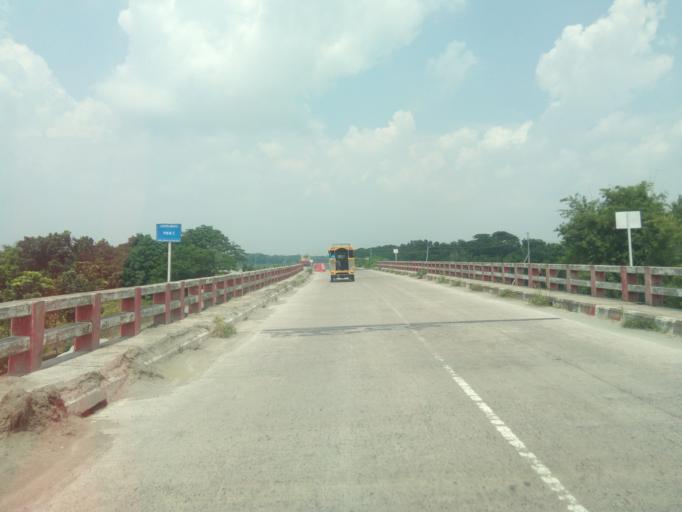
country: BD
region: Dhaka
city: Char Bhadrasan
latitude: 23.3825
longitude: 90.1247
